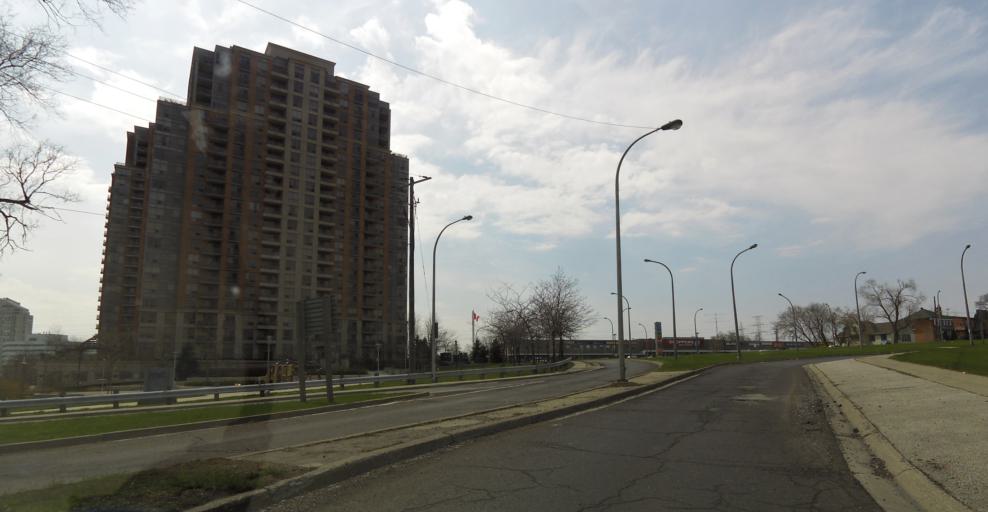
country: CA
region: Ontario
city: Etobicoke
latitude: 43.6399
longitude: -79.5352
